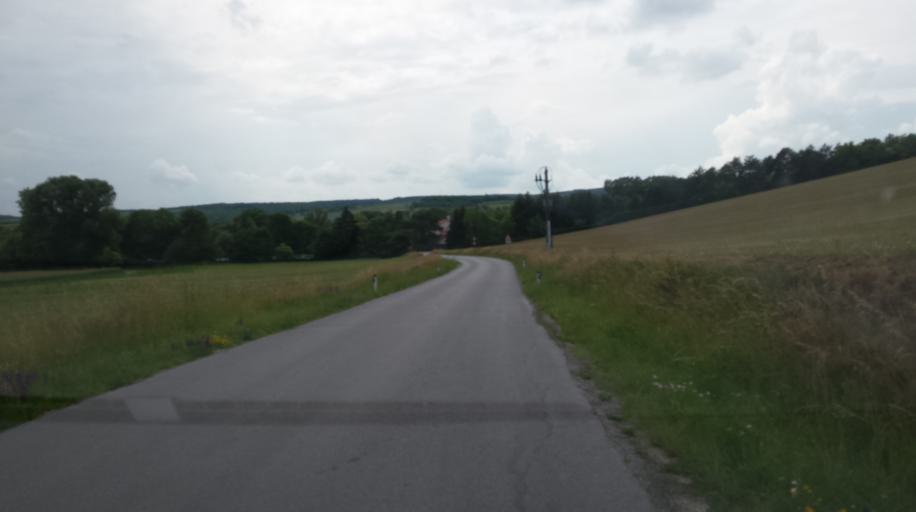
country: AT
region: Lower Austria
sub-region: Politischer Bezirk Mistelbach
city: Wolkersdorf im Weinviertel
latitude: 48.4145
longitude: 16.5046
